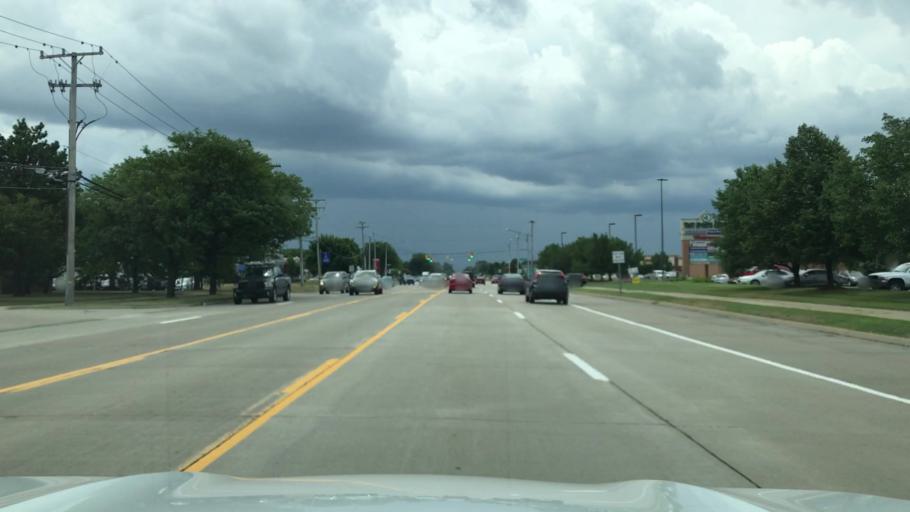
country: US
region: Michigan
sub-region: Oakland County
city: Clawson
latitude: 42.5656
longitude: -83.1084
